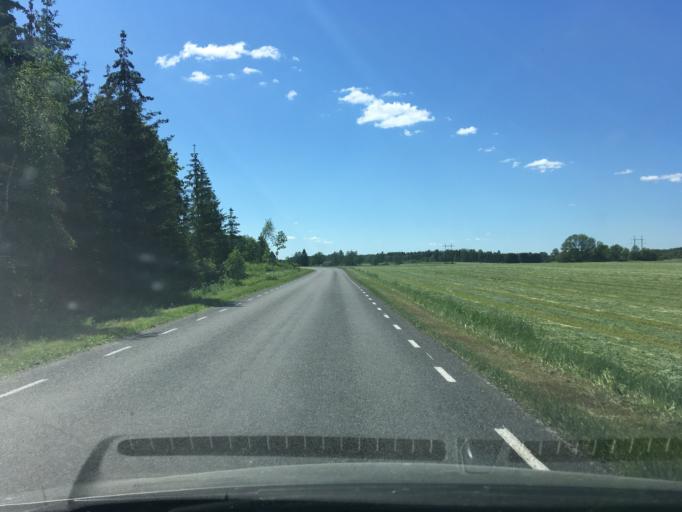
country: EE
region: Raplamaa
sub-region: Kohila vald
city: Kohila
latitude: 59.1381
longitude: 24.8447
